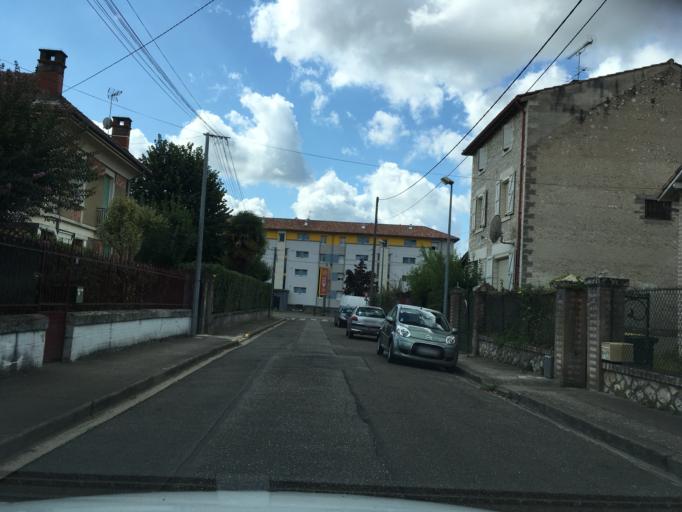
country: FR
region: Aquitaine
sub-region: Departement du Lot-et-Garonne
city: Agen
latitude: 44.2018
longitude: 0.6328
